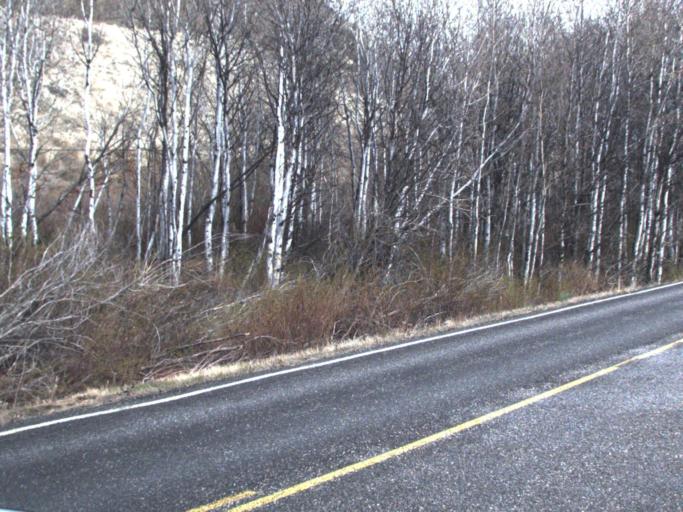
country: US
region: Washington
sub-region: Yakima County
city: Tieton
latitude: 46.7487
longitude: -120.8001
